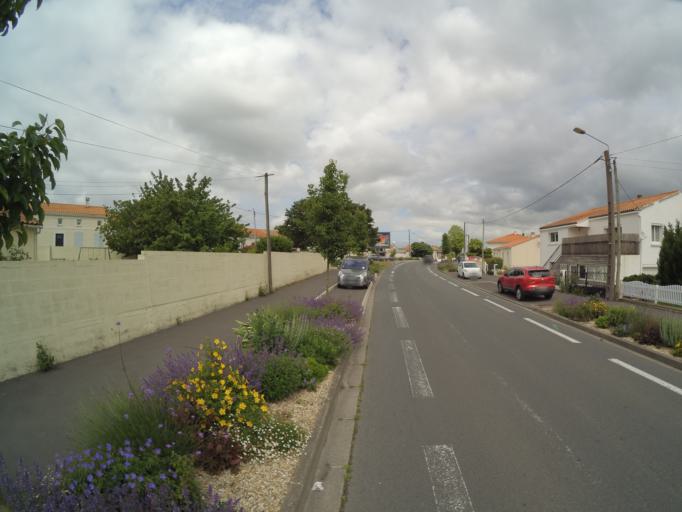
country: FR
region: Poitou-Charentes
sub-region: Departement de la Charente-Maritime
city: Rochefort
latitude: 45.9516
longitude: -0.9682
